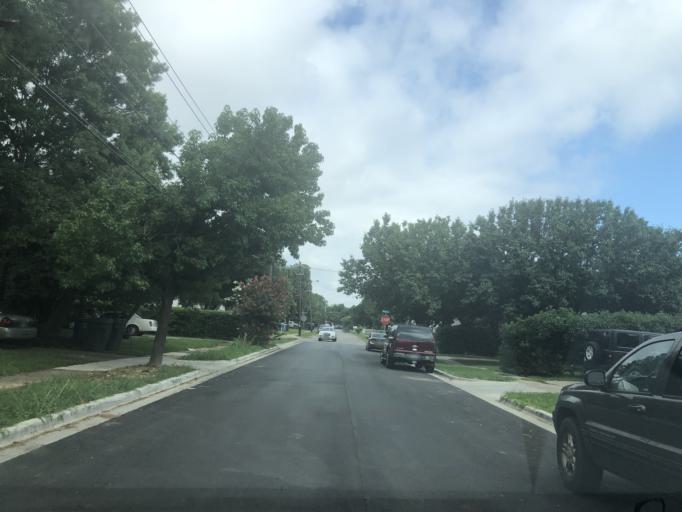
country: US
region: Texas
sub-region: Dallas County
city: University Park
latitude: 32.8662
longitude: -96.8522
